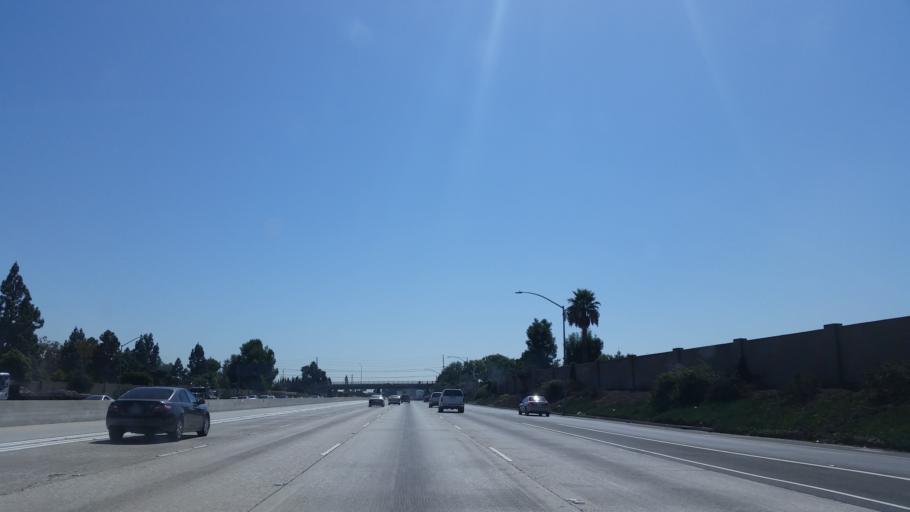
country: US
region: California
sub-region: Los Angeles County
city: Artesia
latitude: 33.8567
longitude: -118.0960
